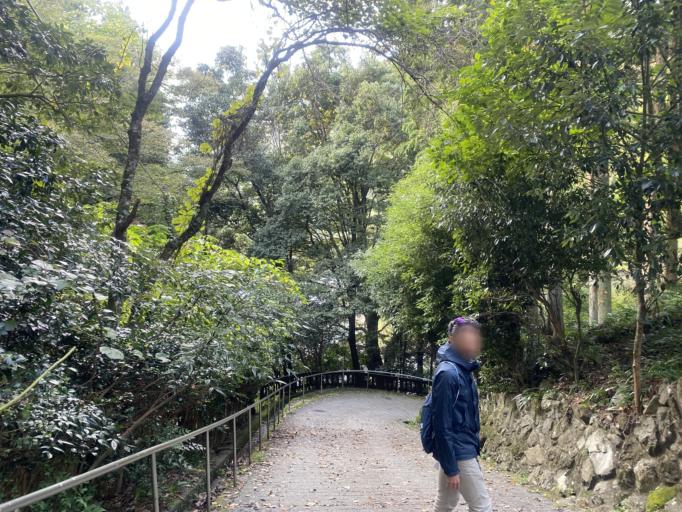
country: JP
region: Shizuoka
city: Fujinomiya
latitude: 35.3793
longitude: 138.4270
